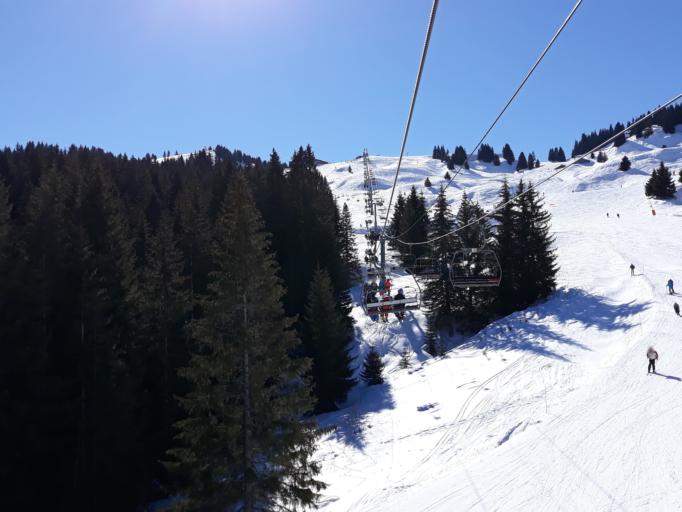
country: FR
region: Rhone-Alpes
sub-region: Departement de la Haute-Savoie
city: Araches-la-Frasse
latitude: 46.0504
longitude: 6.6696
